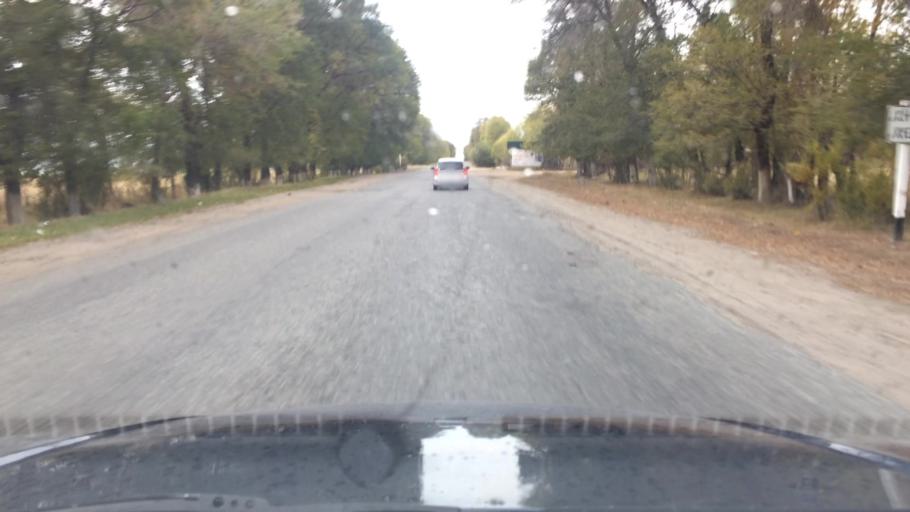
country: KG
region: Ysyk-Koel
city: Tyup
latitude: 42.7368
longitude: 77.9909
